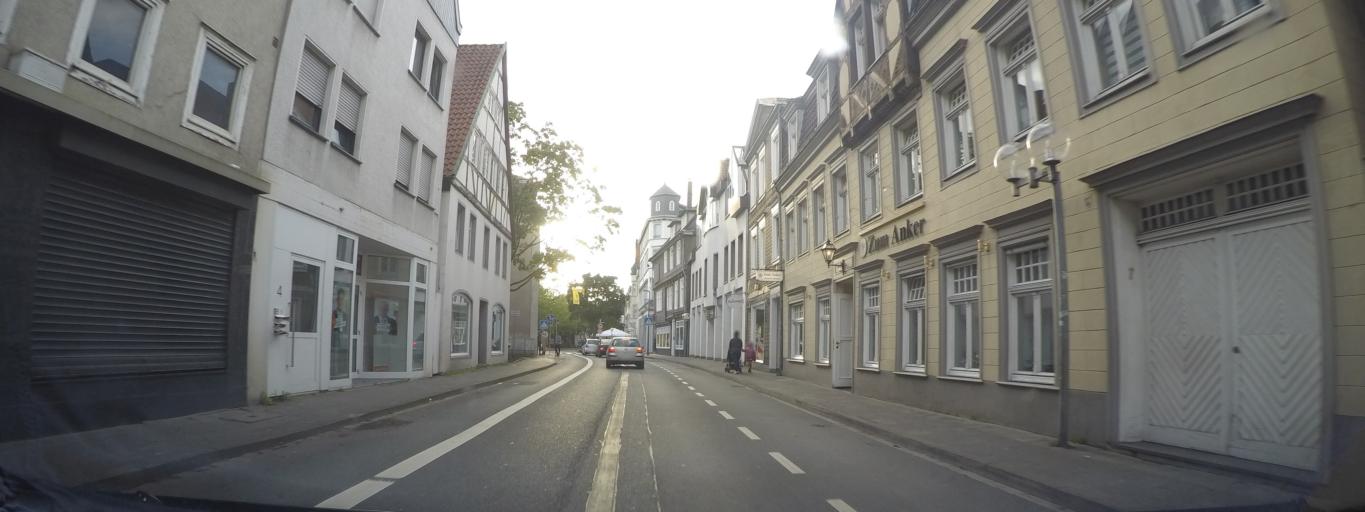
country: DE
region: North Rhine-Westphalia
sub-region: Regierungsbezirk Arnsberg
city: Lippstadt
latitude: 51.6763
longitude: 8.3474
